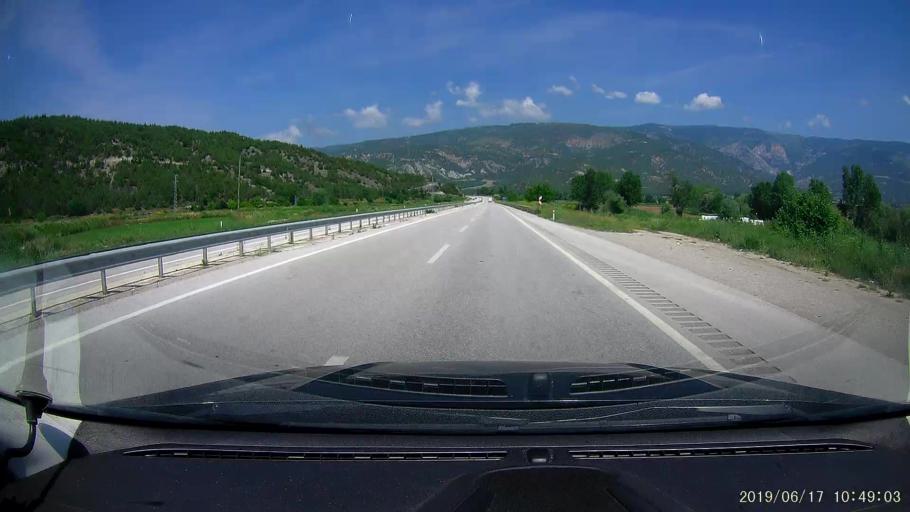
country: TR
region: Corum
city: Hacihamza
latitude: 41.0968
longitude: 34.4183
